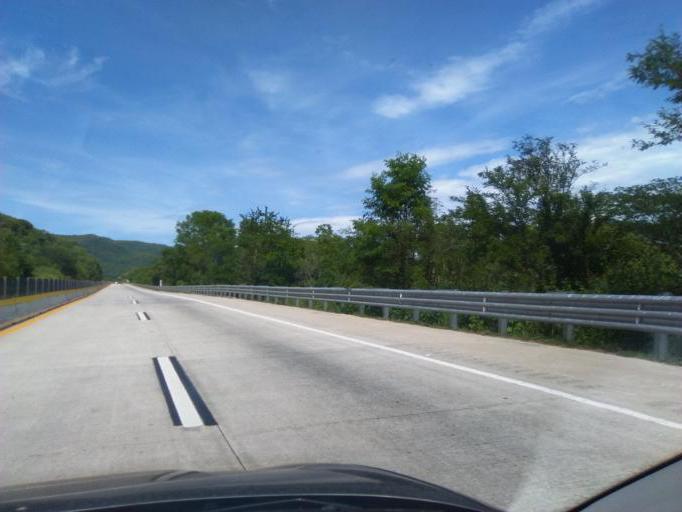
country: MX
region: Guerrero
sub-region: Acapulco de Juarez
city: Pueblo Madero (El Playon)
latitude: 17.0518
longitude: -99.6305
